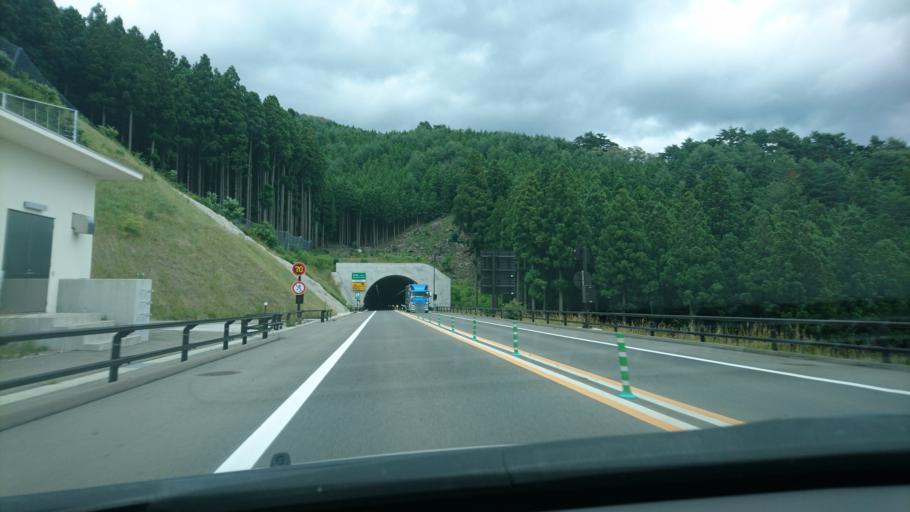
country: JP
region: Iwate
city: Ofunato
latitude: 39.1307
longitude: 141.8052
